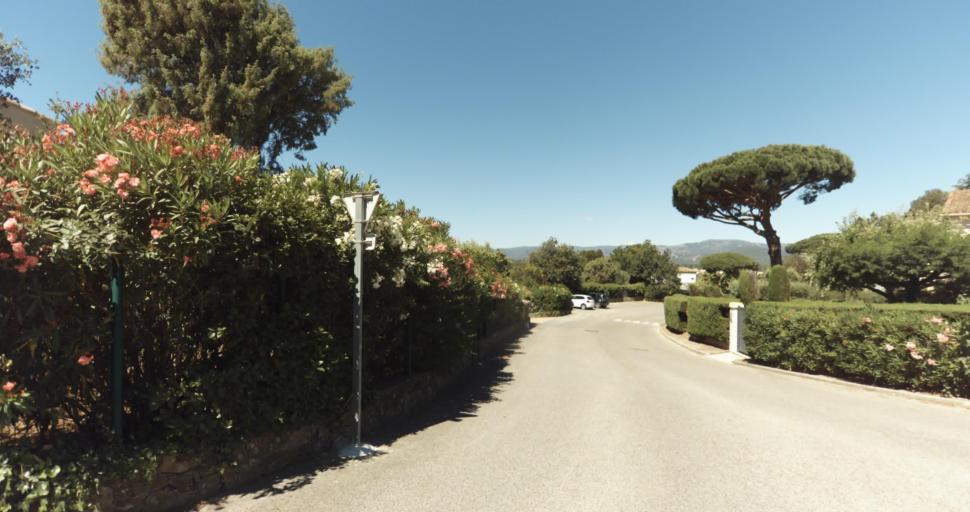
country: FR
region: Provence-Alpes-Cote d'Azur
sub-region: Departement du Var
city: Gassin
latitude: 43.2601
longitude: 6.5998
